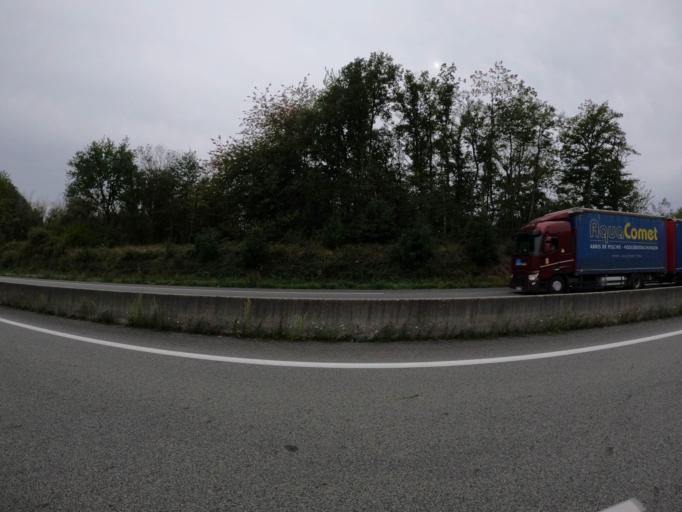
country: FR
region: Limousin
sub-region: Departement de la Creuse
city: Le Grand-Bourg
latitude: 46.2186
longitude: 1.6252
